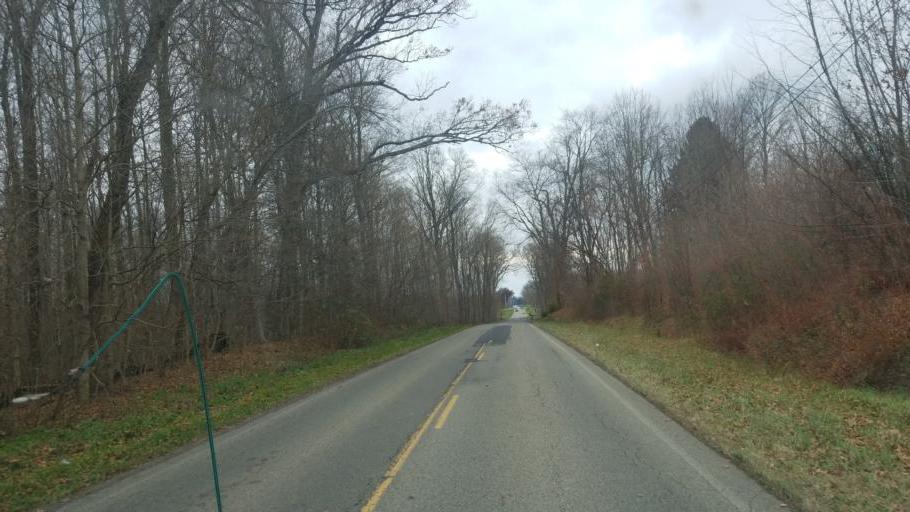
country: US
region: Ohio
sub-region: Knox County
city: Fredericktown
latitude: 40.4613
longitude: -82.5211
